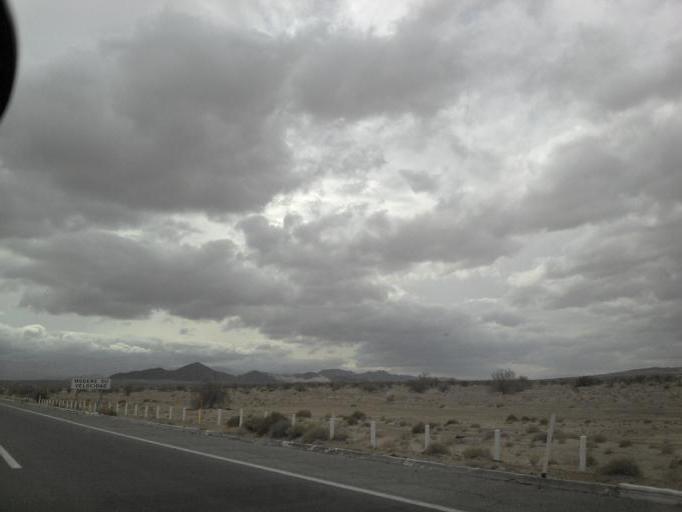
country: MX
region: Baja California
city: Progreso
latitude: 32.5730
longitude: -115.7842
